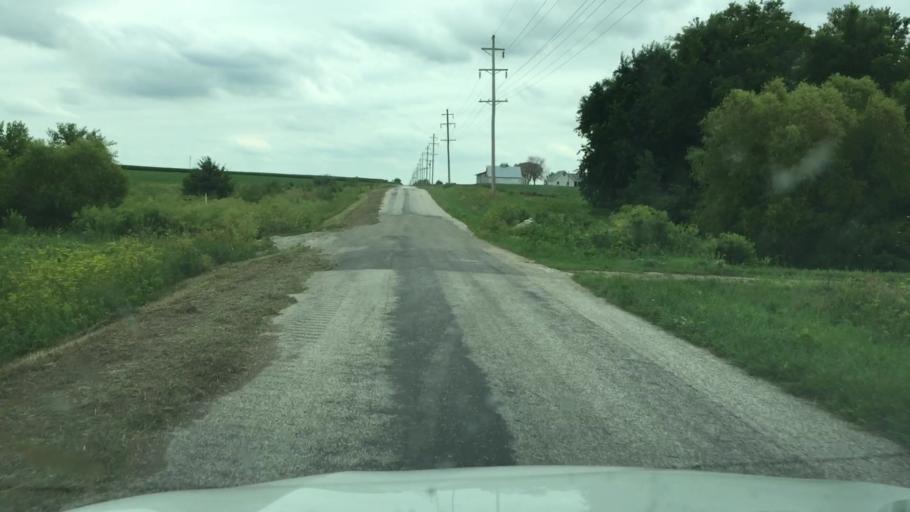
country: US
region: Illinois
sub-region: Hancock County
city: Carthage
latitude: 40.3456
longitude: -91.0822
